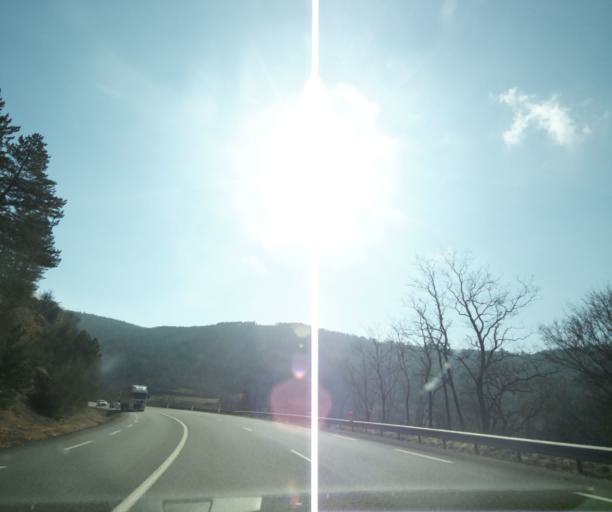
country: FR
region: Languedoc-Roussillon
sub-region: Departement de la Lozere
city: Mende
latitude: 44.4822
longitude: 3.4260
